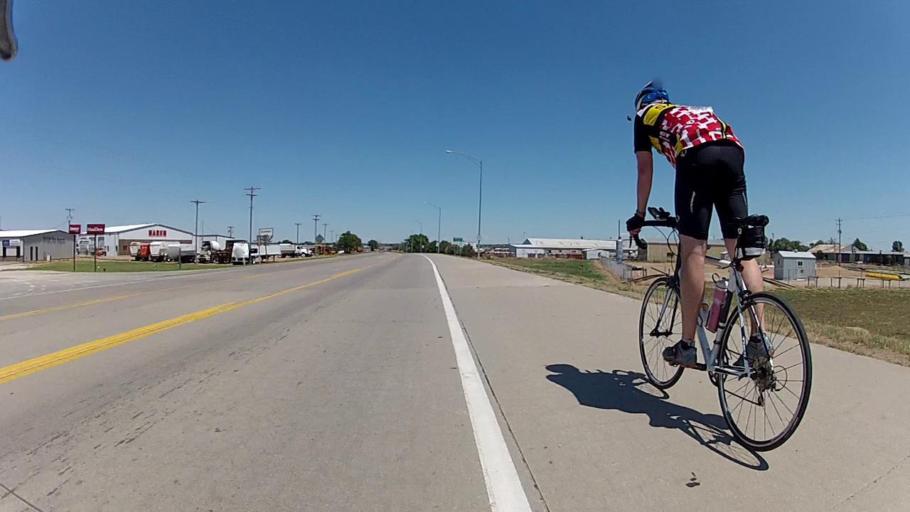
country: US
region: Kansas
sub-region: Ford County
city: Dodge City
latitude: 37.7245
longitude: -100.0158
